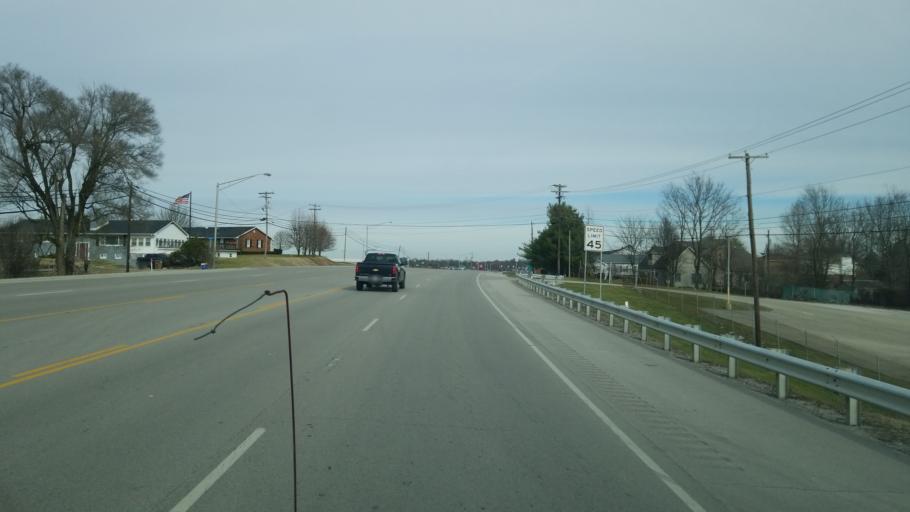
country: US
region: Ohio
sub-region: Brown County
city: Aberdeen
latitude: 38.6285
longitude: -83.7996
